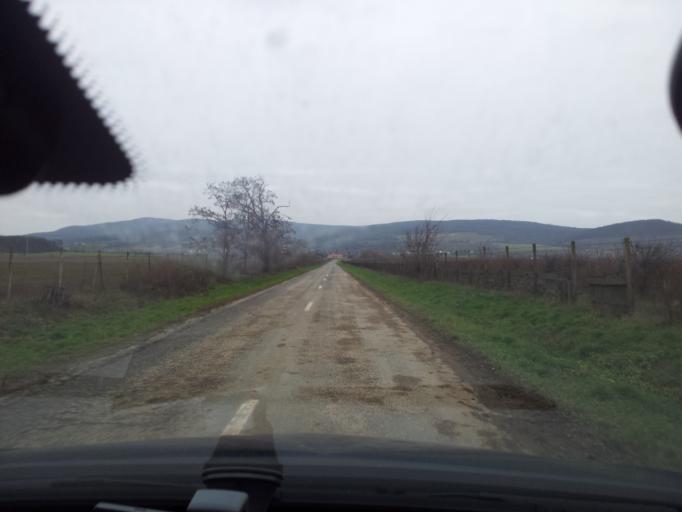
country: HU
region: Borsod-Abauj-Zemplen
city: Satoraljaujhely
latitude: 48.4485
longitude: 21.6635
